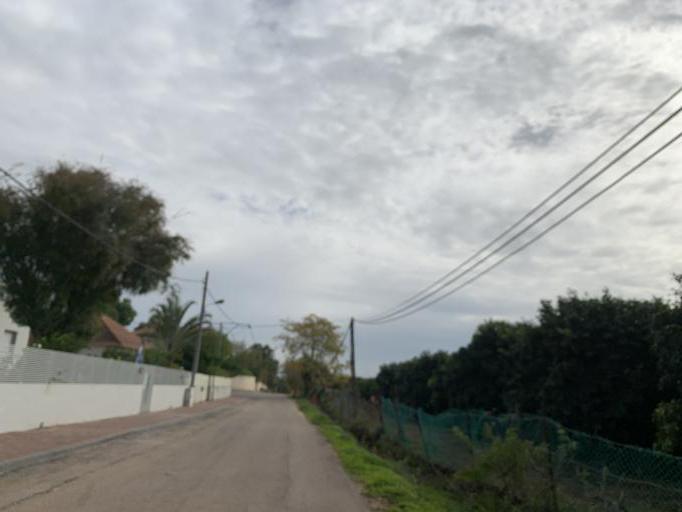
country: IL
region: Central District
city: Hod HaSharon
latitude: 32.1498
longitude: 34.9018
